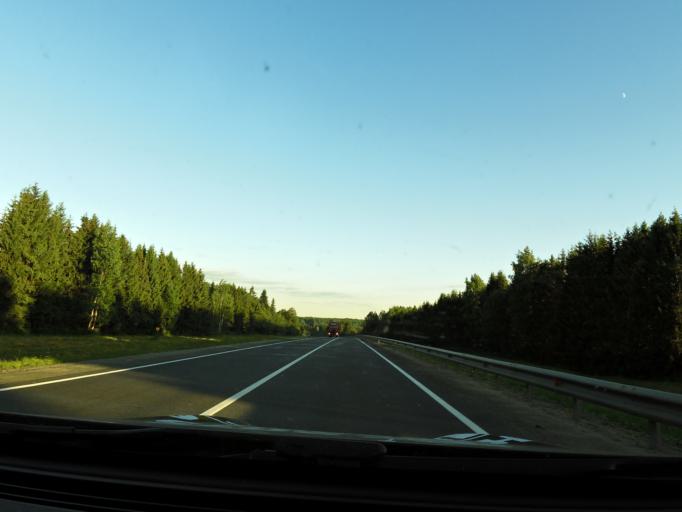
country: RU
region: Vologda
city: Gryazovets
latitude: 58.7040
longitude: 40.2975
